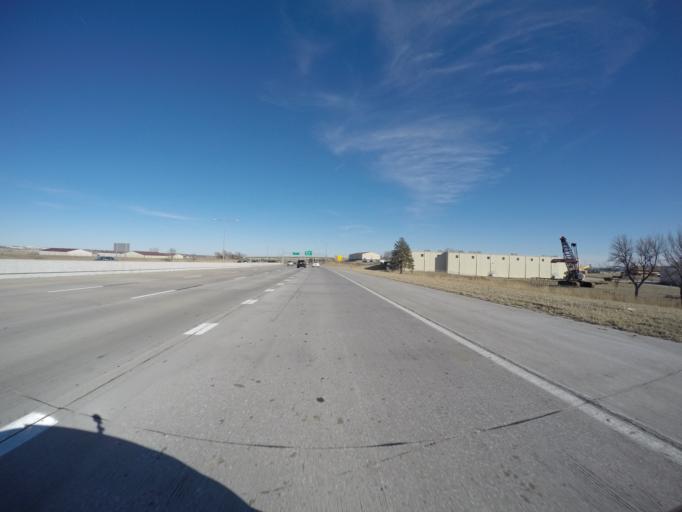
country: US
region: Nebraska
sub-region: Lancaster County
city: Lincoln
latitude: 40.8158
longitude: -96.7627
